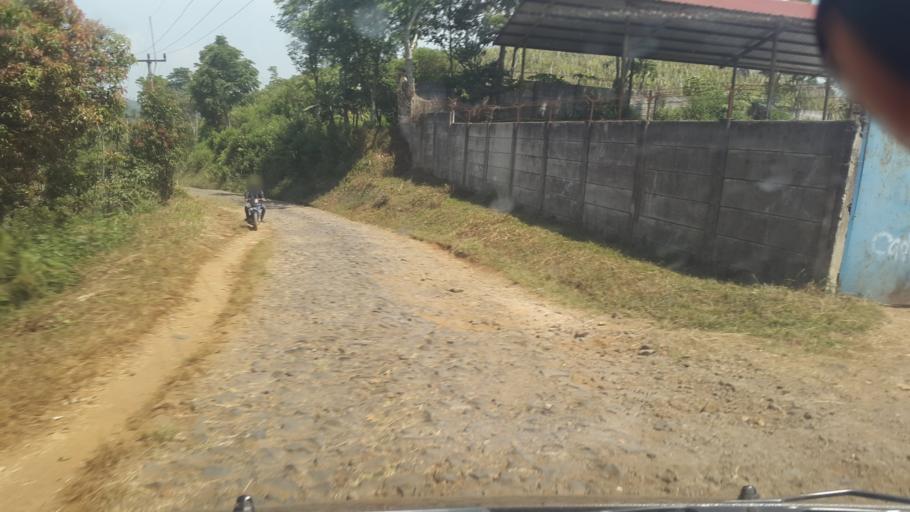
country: ID
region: West Java
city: Pasirhuni
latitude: -7.0231
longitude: 107.0016
